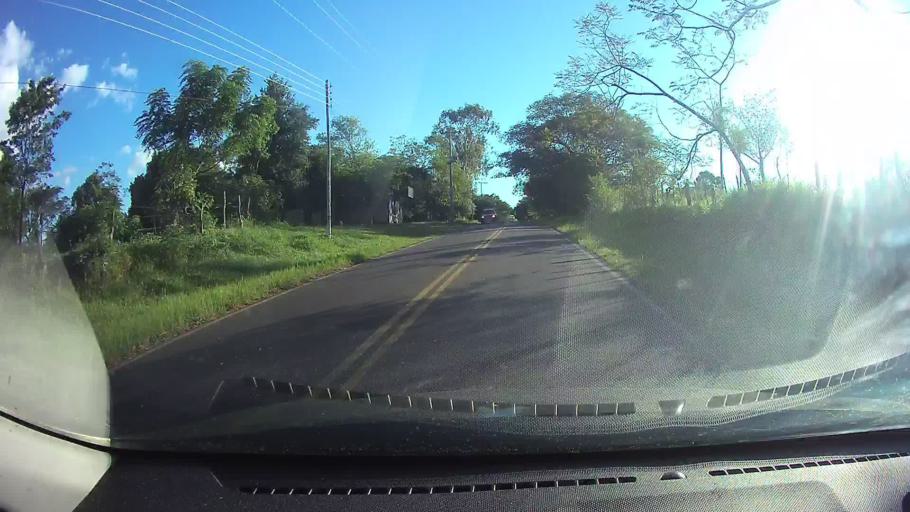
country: PY
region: Cordillera
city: Emboscada
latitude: -25.1995
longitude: -57.3216
